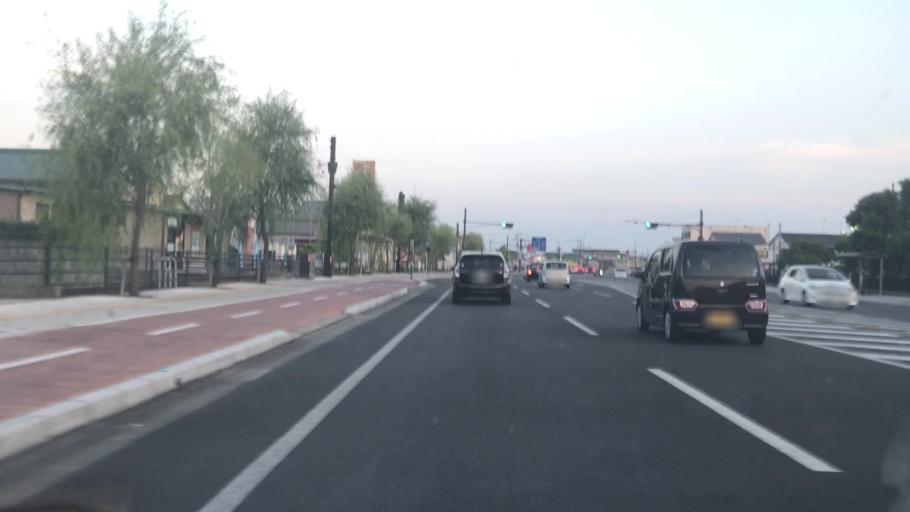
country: JP
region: Saga Prefecture
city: Saga-shi
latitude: 33.2422
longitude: 130.2941
